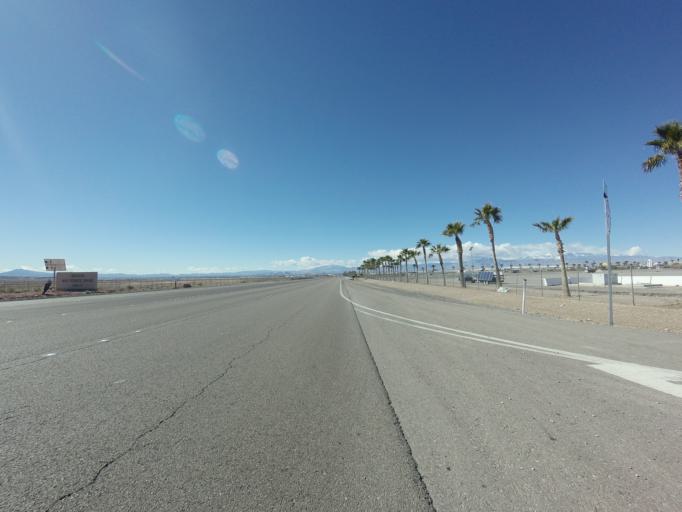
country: US
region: Nevada
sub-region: Clark County
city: Nellis Air Force Base
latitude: 36.2666
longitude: -115.0099
